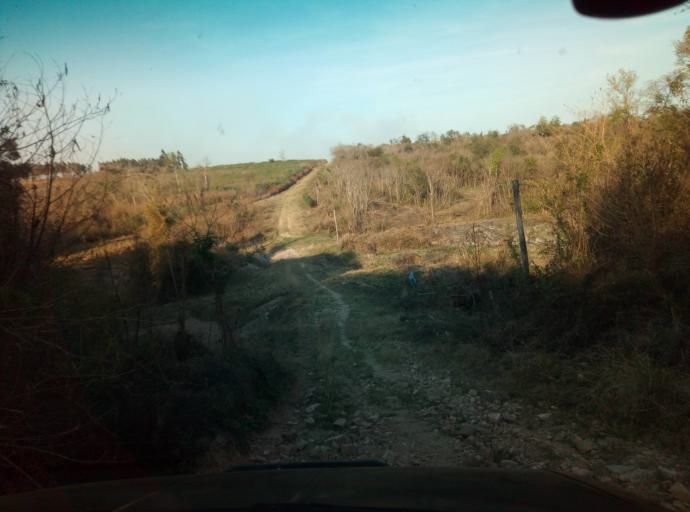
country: PY
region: Caaguazu
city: Doctor Cecilio Baez
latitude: -25.2002
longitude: -56.1264
